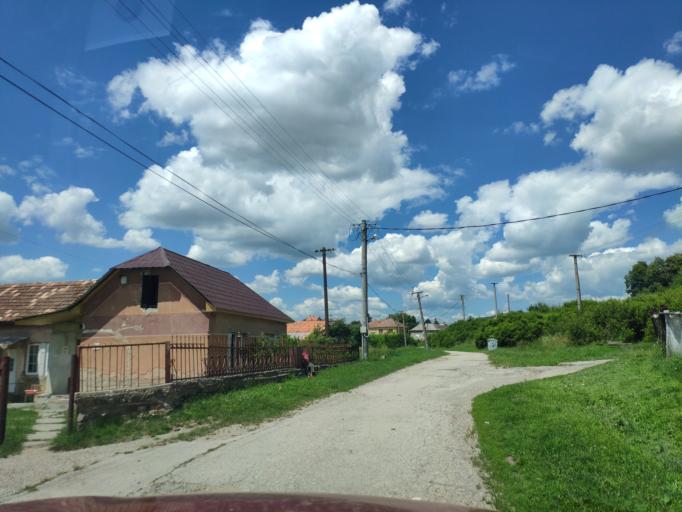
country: HU
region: Borsod-Abauj-Zemplen
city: Ozd
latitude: 48.3032
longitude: 20.2329
